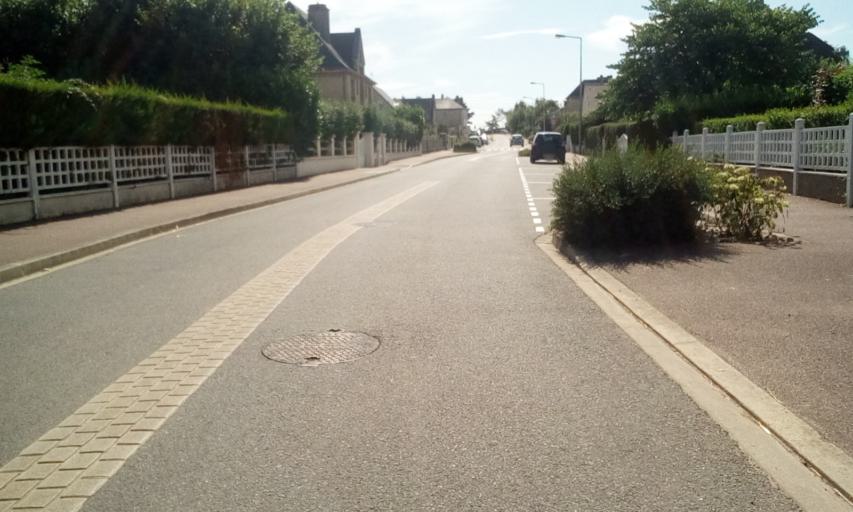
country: FR
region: Lower Normandy
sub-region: Departement du Calvados
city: Eterville
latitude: 49.1298
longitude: -0.4213
